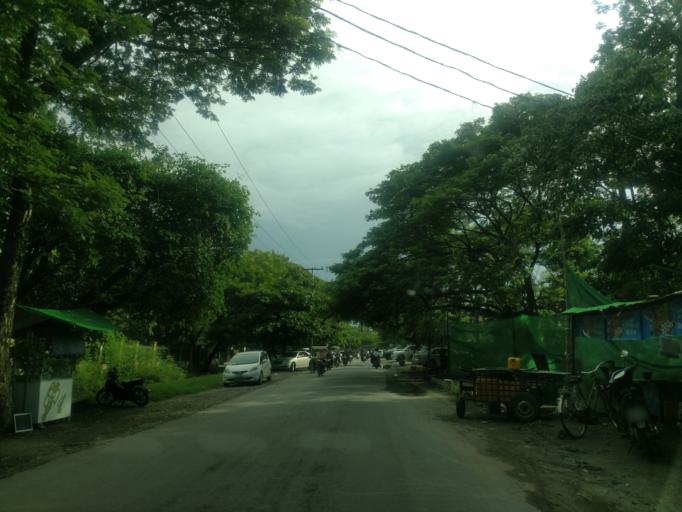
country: MM
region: Mandalay
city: Mandalay
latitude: 21.9788
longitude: 96.1006
